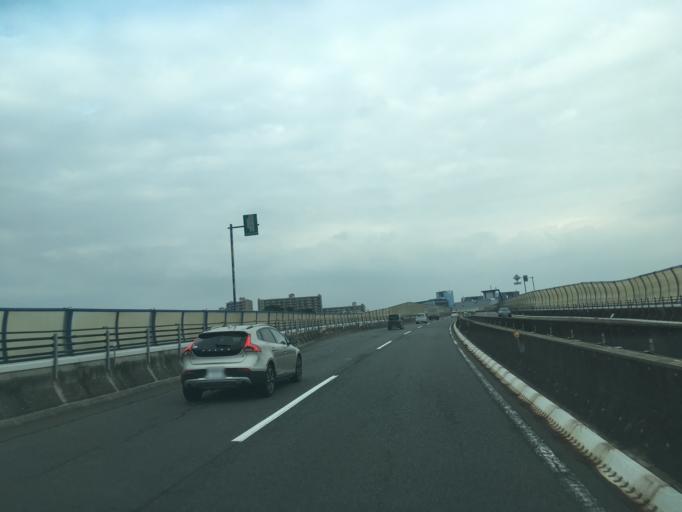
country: JP
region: Kanagawa
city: Chigasaki
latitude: 35.3273
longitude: 139.3785
